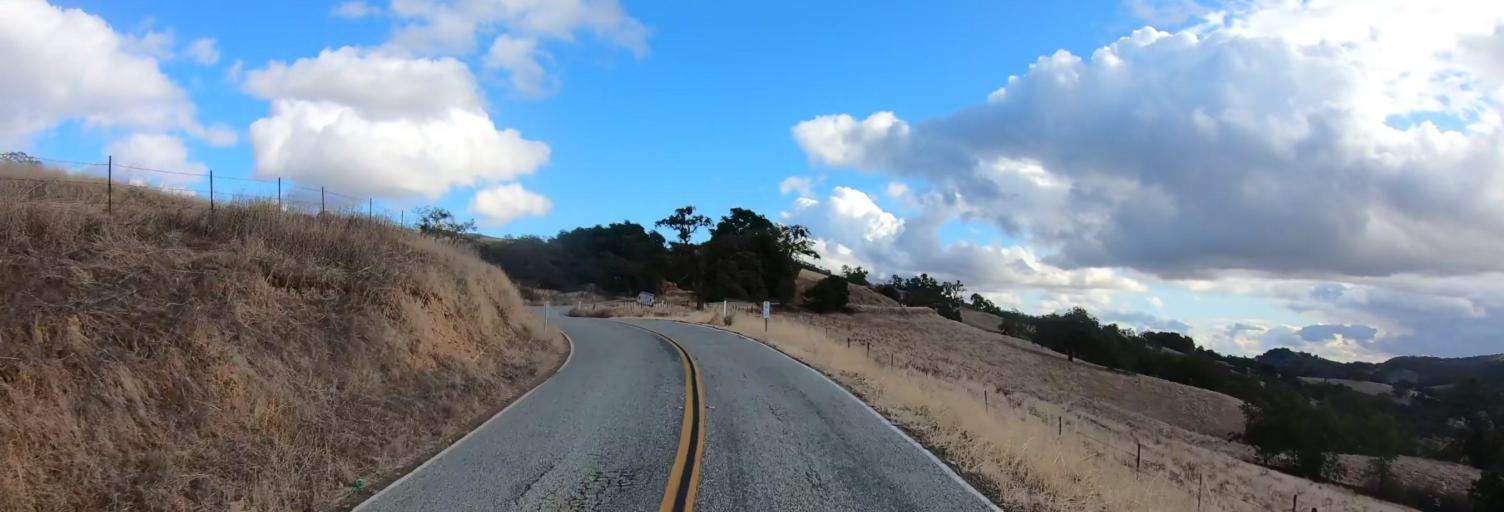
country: US
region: California
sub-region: Santa Clara County
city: East Foothills
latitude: 37.3400
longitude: -121.7113
